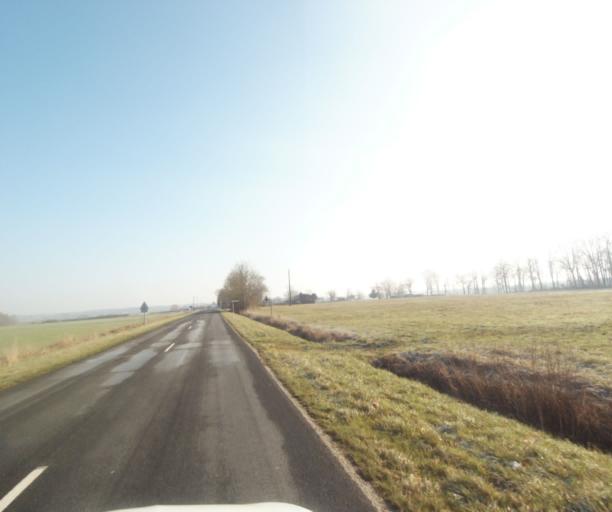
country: FR
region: Champagne-Ardenne
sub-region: Departement de la Haute-Marne
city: Laneuville-a-Remy
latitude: 48.4930
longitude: 4.8525
